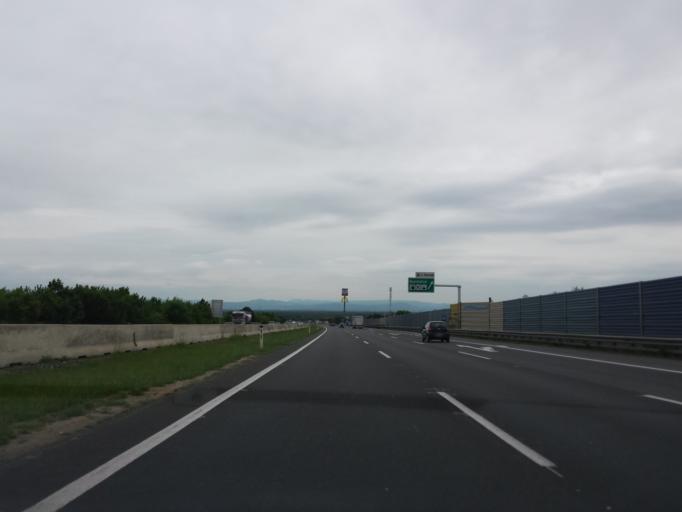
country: AT
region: Lower Austria
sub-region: Politischer Bezirk Wiener Neustadt
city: Weikersdorf am Steinfelde
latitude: 47.8393
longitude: 16.1816
